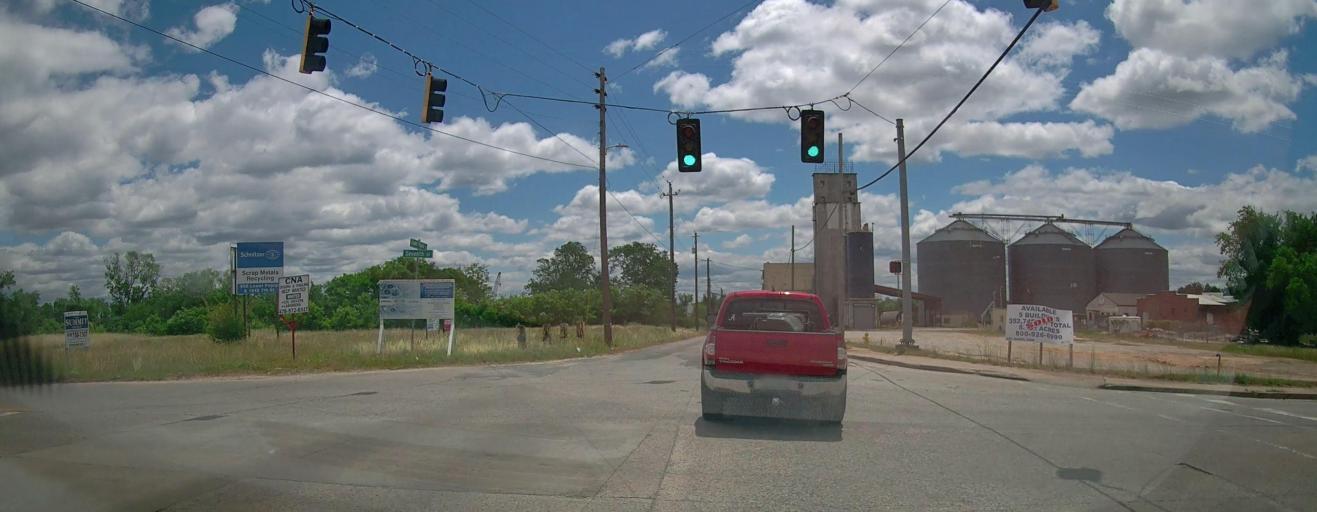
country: US
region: Georgia
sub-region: Bibb County
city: Macon
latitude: 32.8303
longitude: -83.6225
